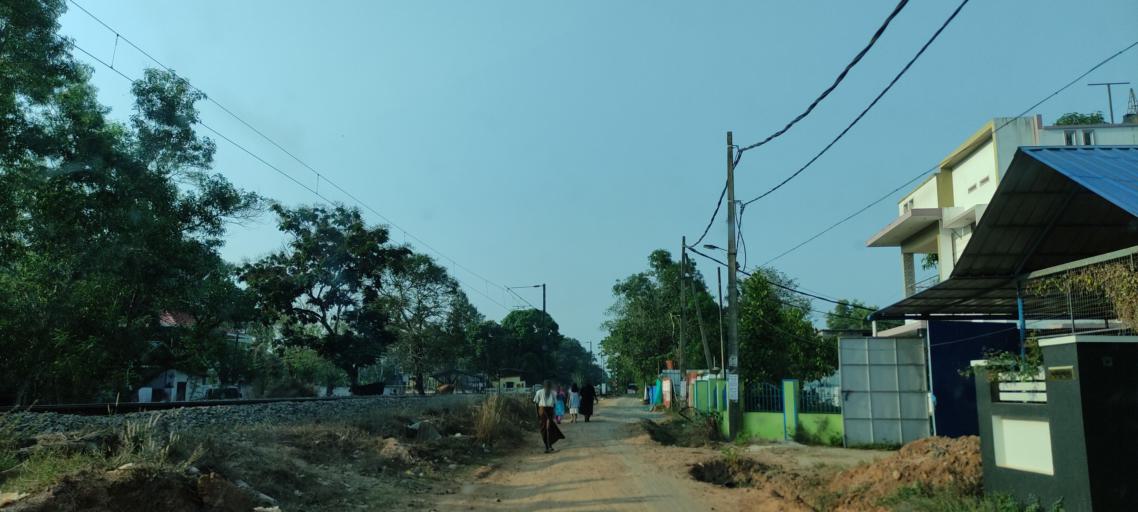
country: IN
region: Kerala
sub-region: Alappuzha
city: Alleppey
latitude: 9.5276
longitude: 76.3215
